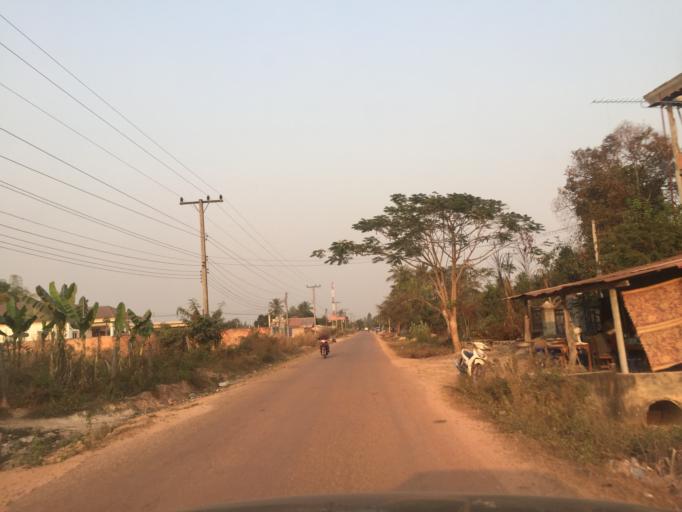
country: TH
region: Nong Khai
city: Si Chiang Mai
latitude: 18.0562
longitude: 102.5171
